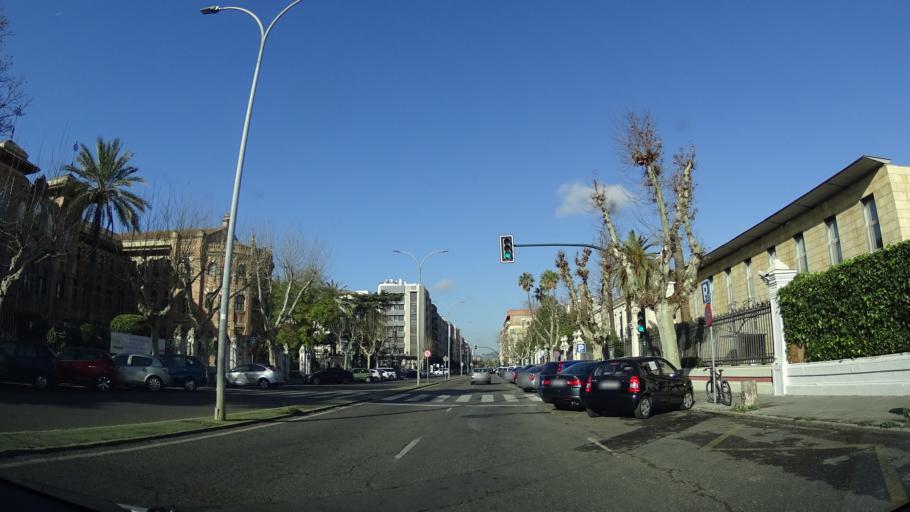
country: ES
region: Andalusia
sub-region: Province of Cordoba
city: Cordoba
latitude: 37.8851
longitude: -4.7880
